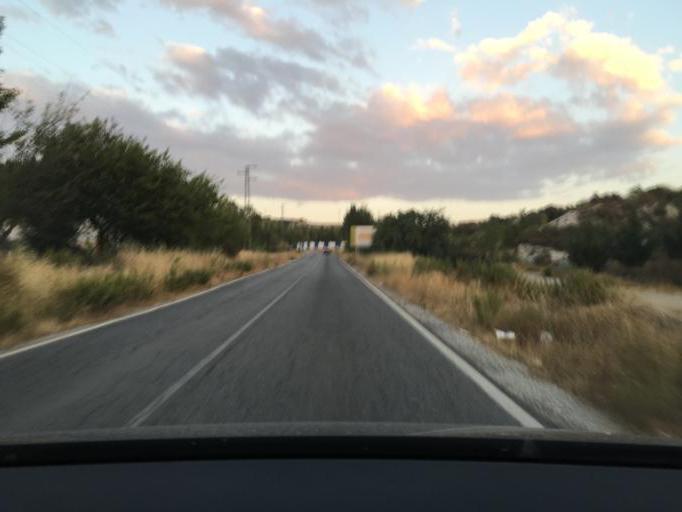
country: ES
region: Andalusia
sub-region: Provincia de Granada
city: Beas de Granada
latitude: 37.2284
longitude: -3.4975
